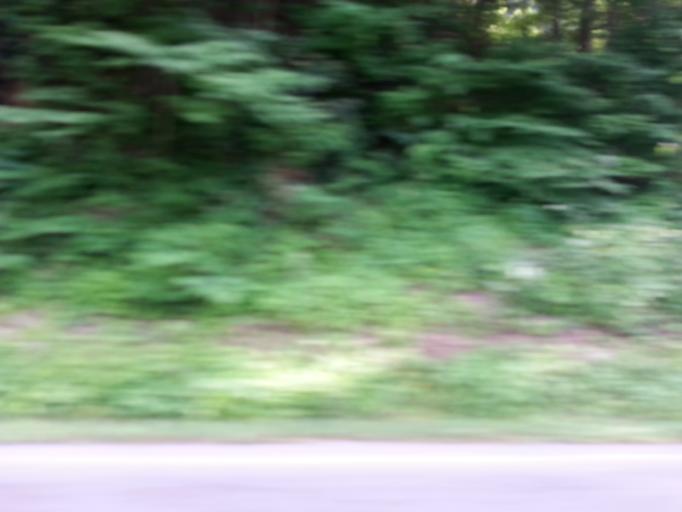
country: US
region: Tennessee
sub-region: Sevier County
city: Gatlinburg
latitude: 35.6728
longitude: -83.5729
